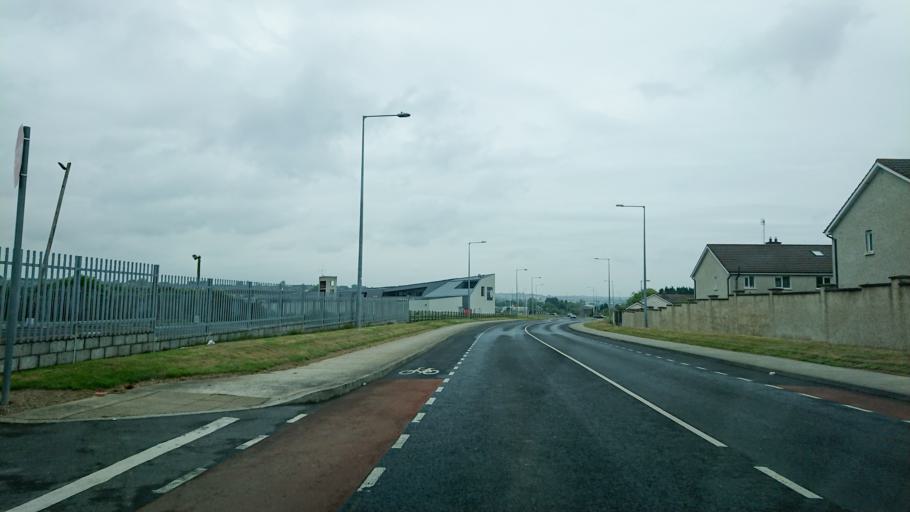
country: IE
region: Munster
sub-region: Waterford
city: Waterford
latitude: 52.2409
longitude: -7.1354
